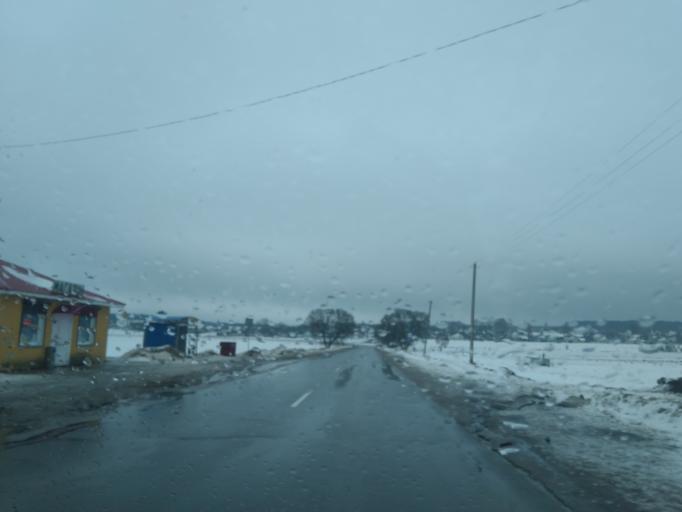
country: BY
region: Minsk
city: Stowbtsy
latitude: 53.5827
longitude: 26.8330
